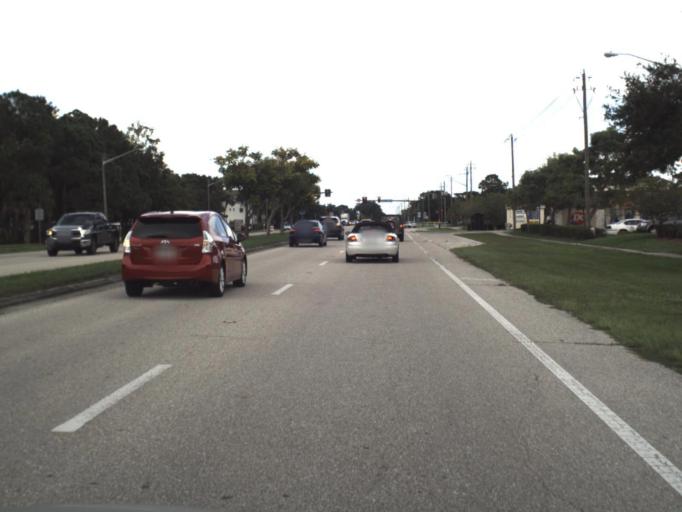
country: US
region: Florida
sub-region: Sarasota County
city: Venice Gardens
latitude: 27.0997
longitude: -82.4150
